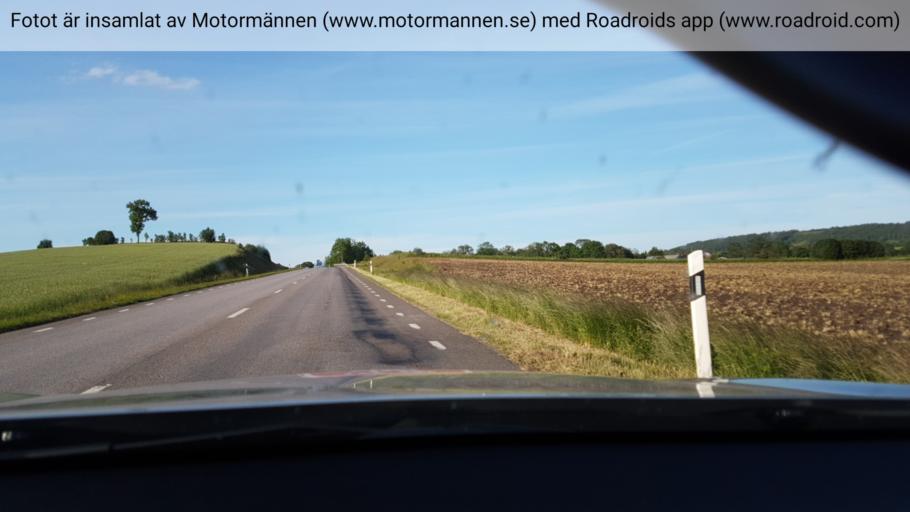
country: SE
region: Vaestra Goetaland
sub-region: Falkopings Kommun
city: Falkoeping
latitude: 58.1290
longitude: 13.5567
